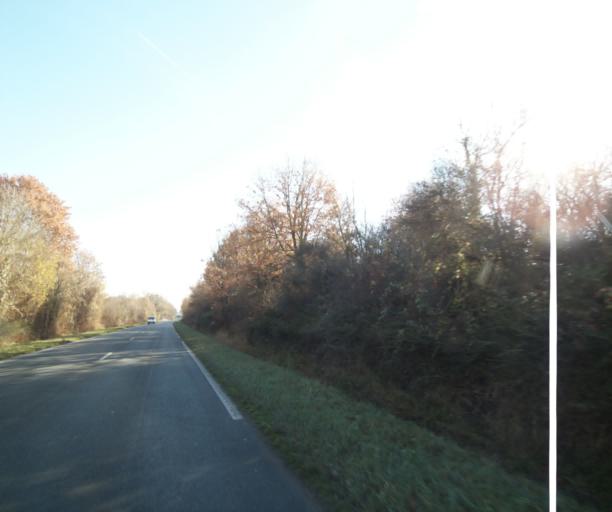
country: FR
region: Poitou-Charentes
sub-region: Departement de la Charente-Maritime
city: Chaniers
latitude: 45.7131
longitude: -0.5409
